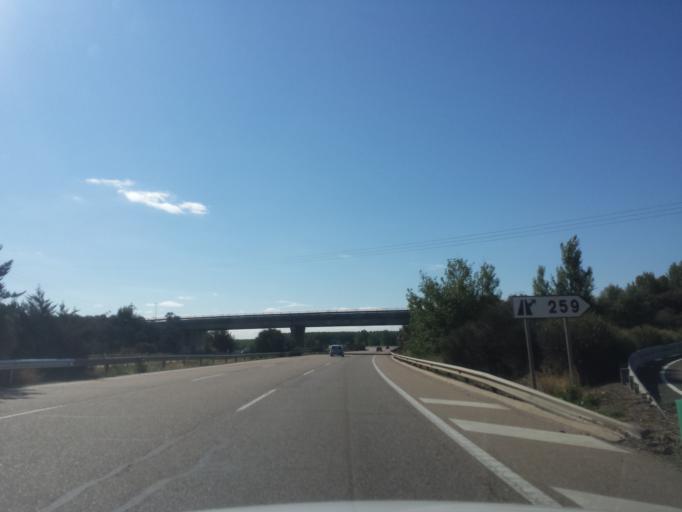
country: ES
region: Castille and Leon
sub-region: Provincia de Zamora
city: Villanueva de Azoague
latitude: 41.9908
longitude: -5.6384
